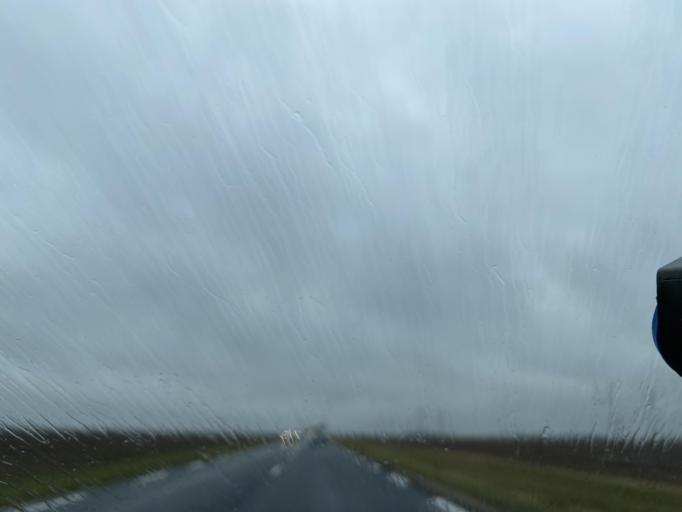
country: FR
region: Centre
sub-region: Departement d'Eure-et-Loir
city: Janville
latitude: 48.1854
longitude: 1.8315
